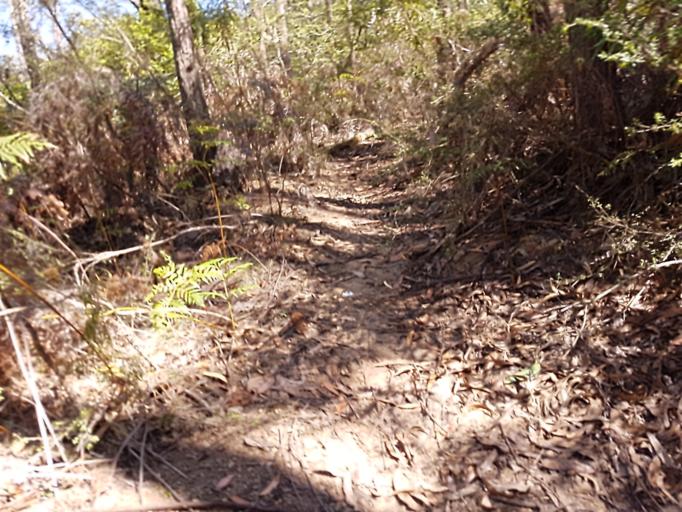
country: AU
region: Victoria
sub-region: East Gippsland
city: Lakes Entrance
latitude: -37.2207
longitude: 148.2817
